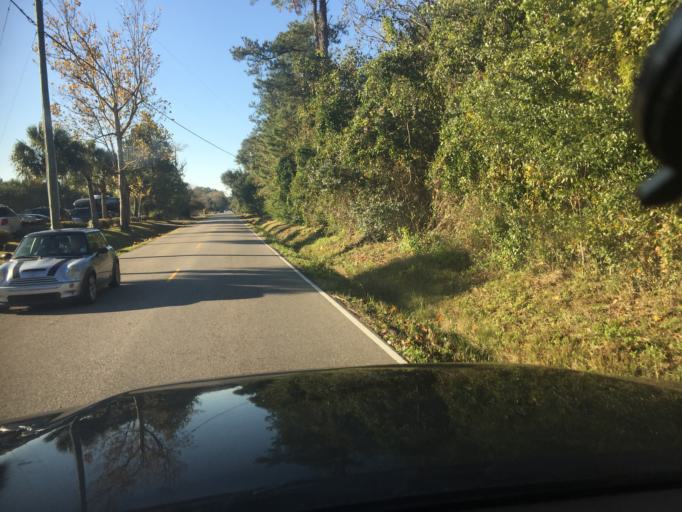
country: US
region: Louisiana
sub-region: Saint Tammany Parish
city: Slidell
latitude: 30.2517
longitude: -89.7679
